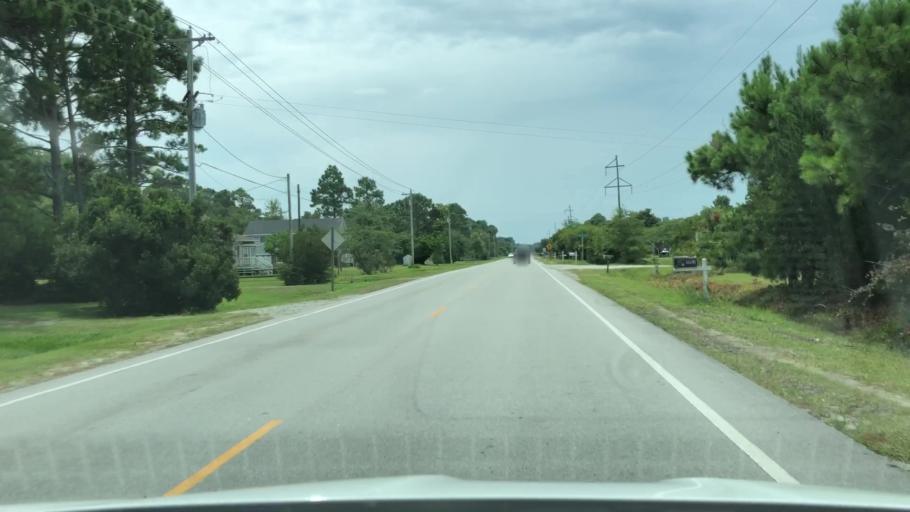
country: US
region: North Carolina
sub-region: Carteret County
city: Newport
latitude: 34.7445
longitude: -76.8818
